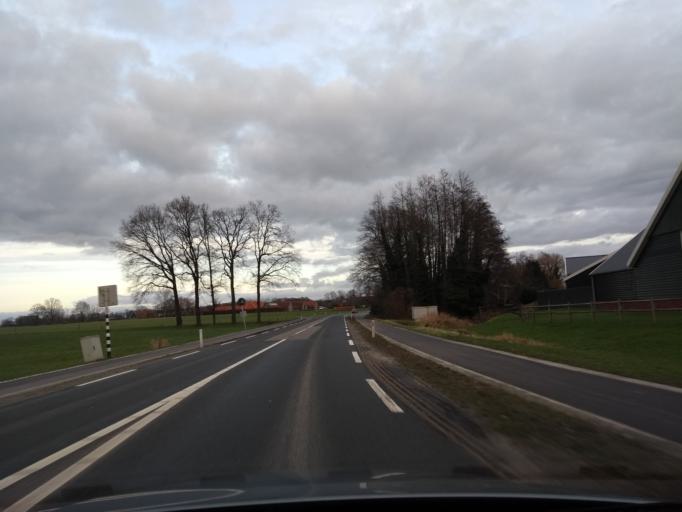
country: NL
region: Overijssel
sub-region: Gemeente Hengelo
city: Hengelo
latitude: 52.3045
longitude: 6.8389
